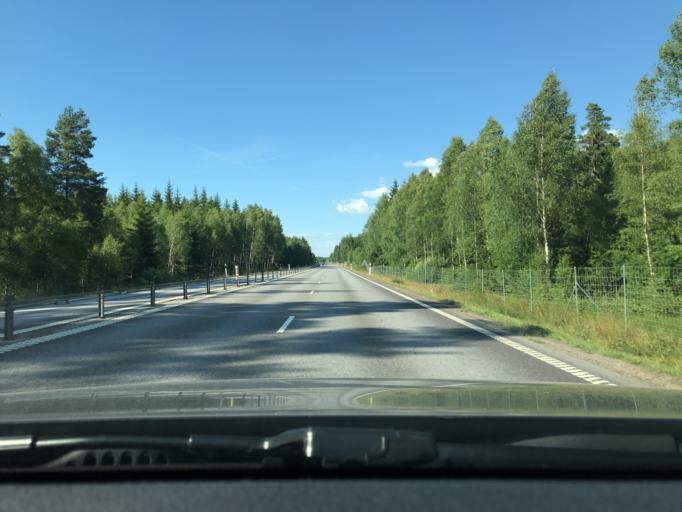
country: SE
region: Skane
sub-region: Osby Kommun
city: Osby
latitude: 56.4185
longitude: 14.0518
